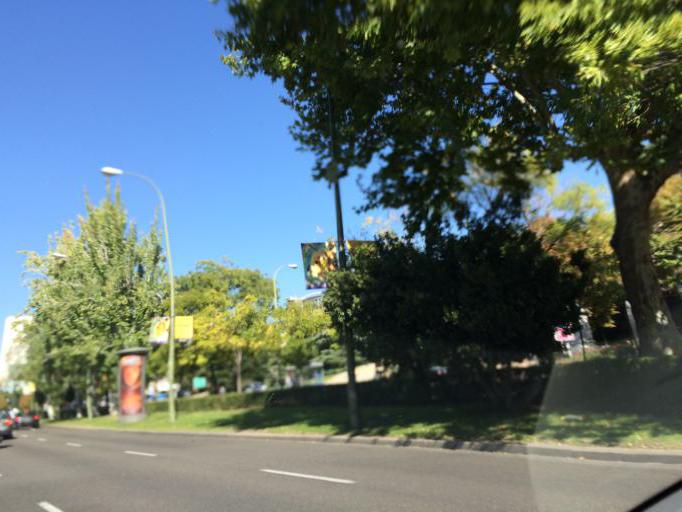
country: ES
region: Madrid
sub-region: Provincia de Madrid
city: Chamberi
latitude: 40.4398
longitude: -3.6913
